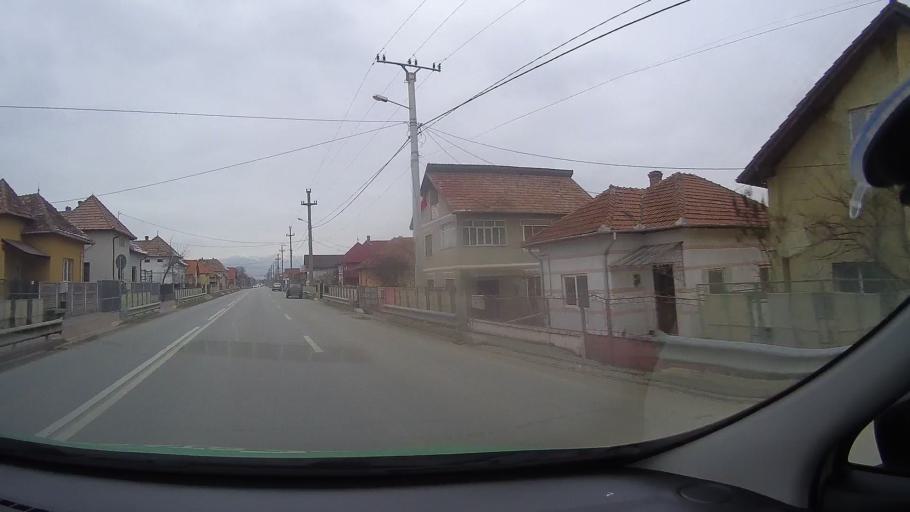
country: RO
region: Alba
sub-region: Municipiul Alba Iulia
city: Micesti
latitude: 46.1007
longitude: 23.5500
